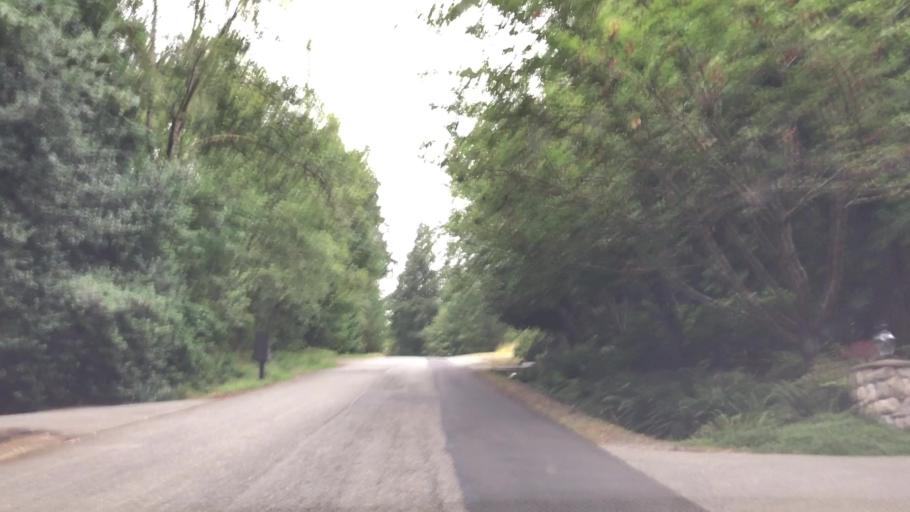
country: US
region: Washington
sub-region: King County
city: Cottage Lake
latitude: 47.7226
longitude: -122.0918
